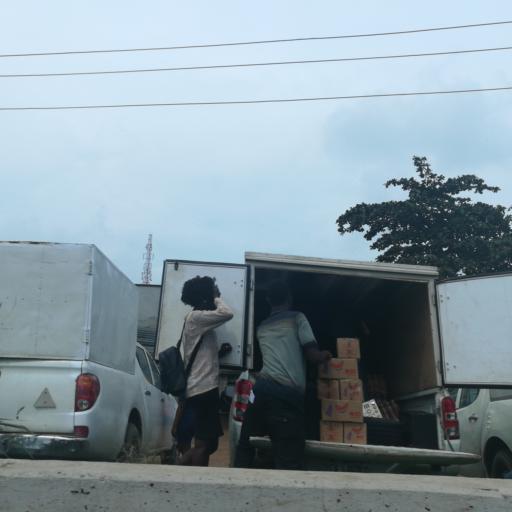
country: NG
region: Lagos
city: Ojota
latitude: 6.5764
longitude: 3.3967
